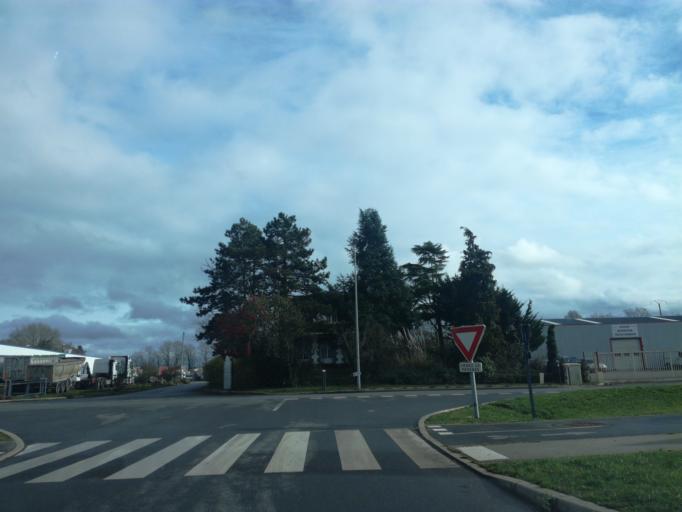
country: FR
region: Brittany
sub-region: Departement du Morbihan
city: Saint-Thuriau
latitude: 48.0376
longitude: -2.9628
